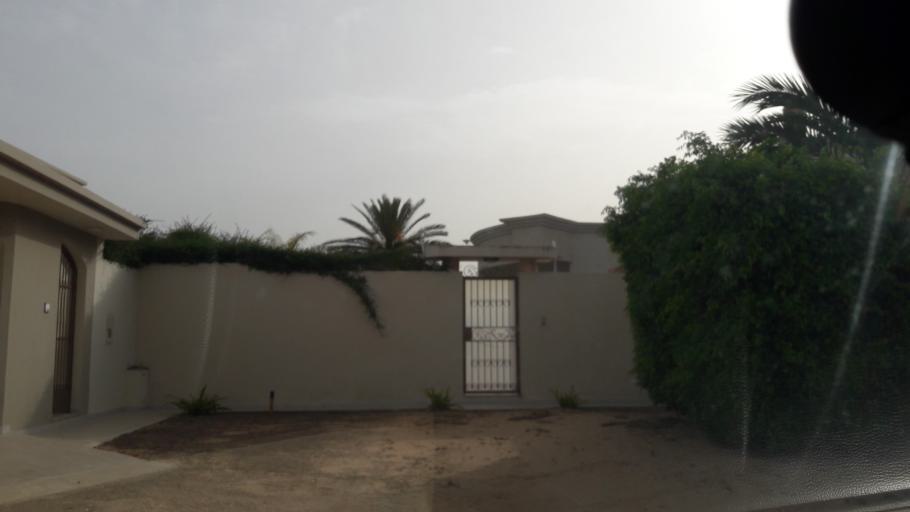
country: TN
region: Safaqis
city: Al Qarmadah
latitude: 34.7787
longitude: 10.7724
